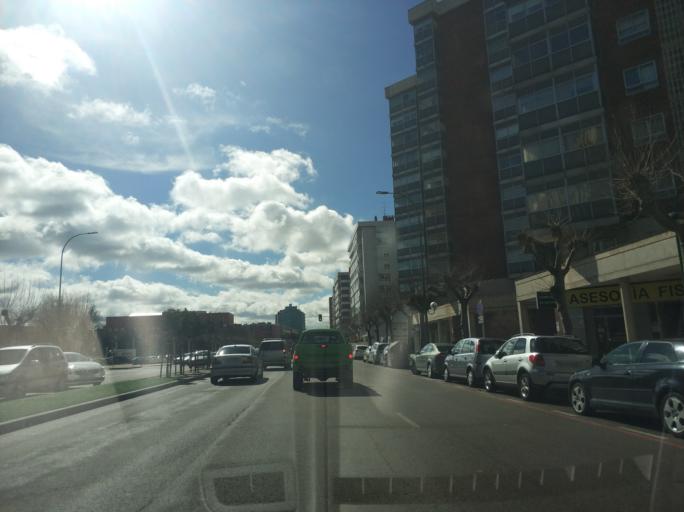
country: ES
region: Castille and Leon
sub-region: Provincia de Burgos
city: Burgos
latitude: 42.3493
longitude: -3.6889
